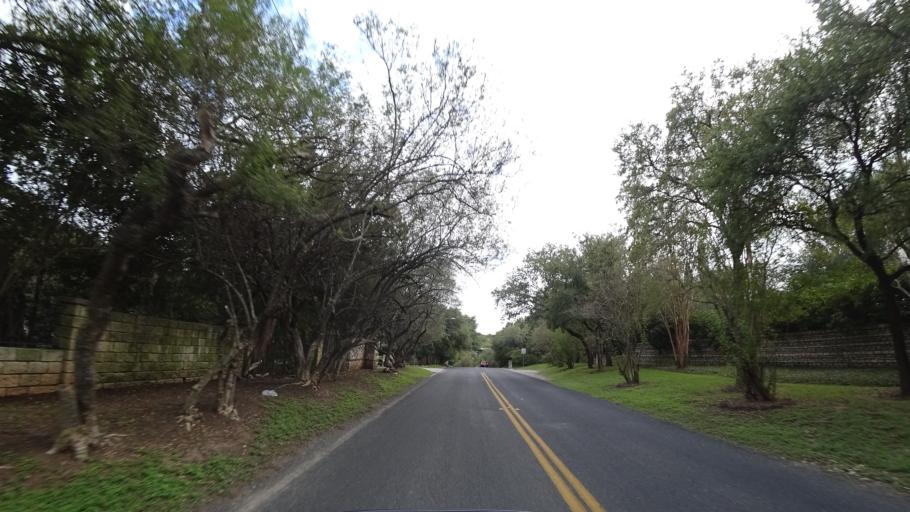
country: US
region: Texas
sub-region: Travis County
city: Rollingwood
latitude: 30.2865
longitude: -97.7891
